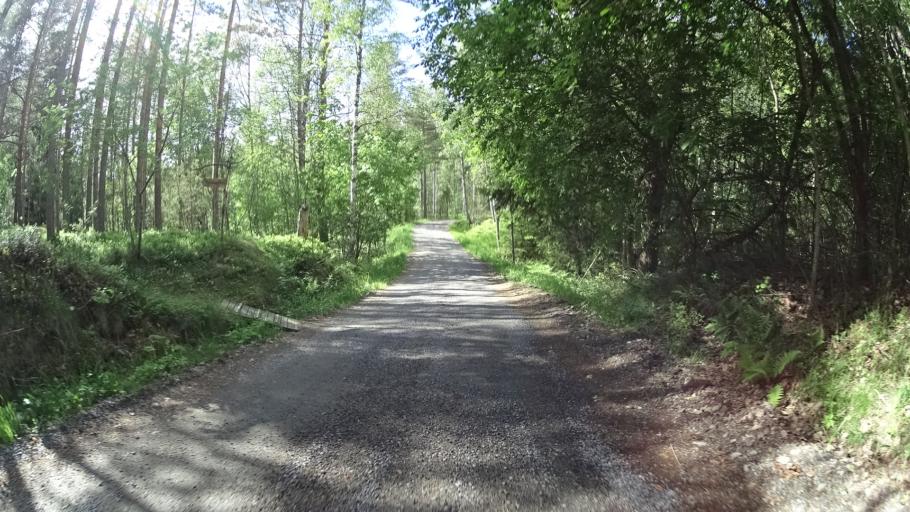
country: FI
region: Varsinais-Suomi
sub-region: Salo
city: Kisko
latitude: 60.1950
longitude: 23.5509
